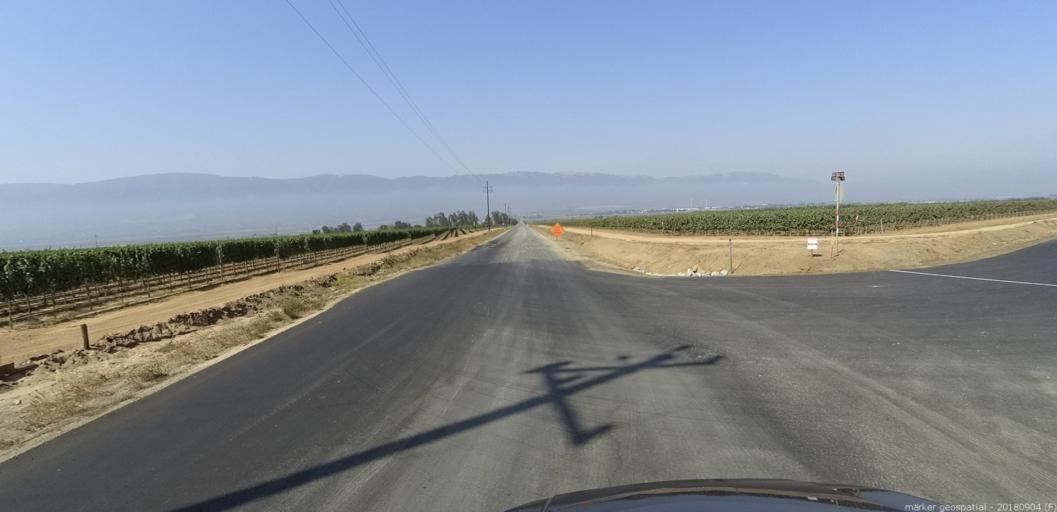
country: US
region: California
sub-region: Monterey County
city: Gonzales
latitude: 36.5017
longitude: -121.3943
